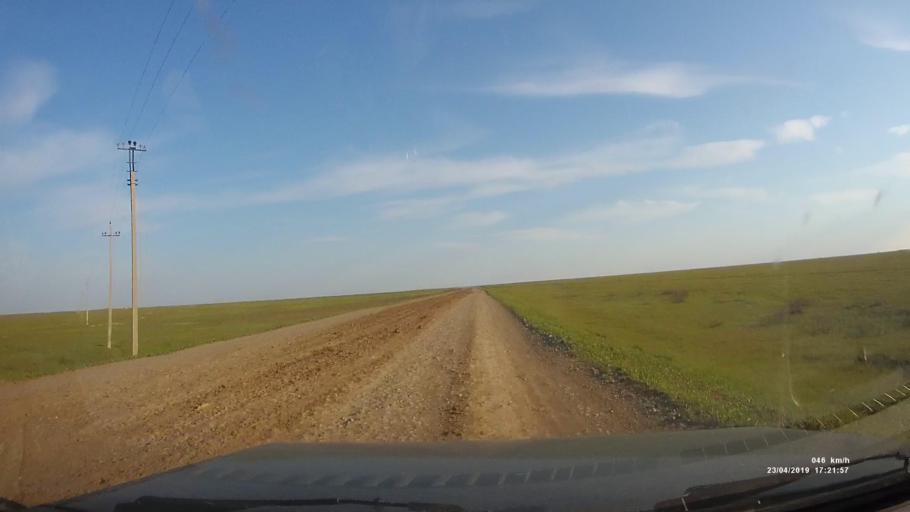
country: RU
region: Kalmykiya
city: Priyutnoye
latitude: 46.1721
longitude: 43.5060
